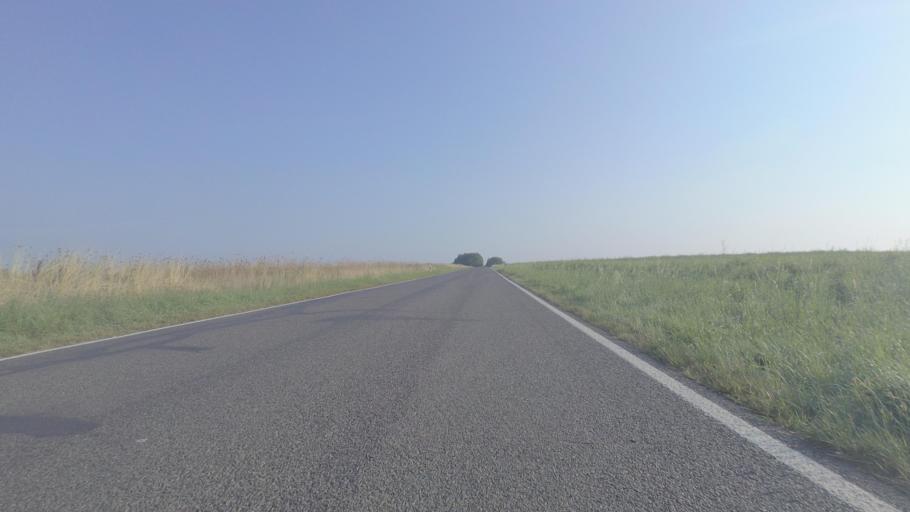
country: DE
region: Brandenburg
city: Heiligengrabe
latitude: 53.2745
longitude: 12.3419
